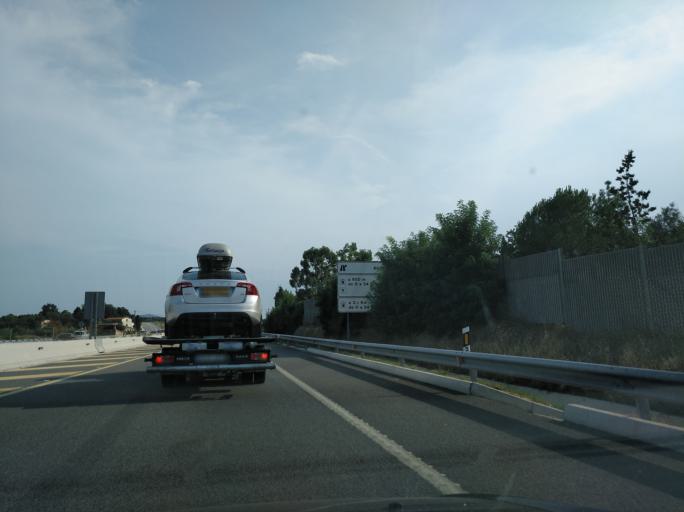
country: ES
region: Catalonia
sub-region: Provincia de Girona
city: Sils
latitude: 41.8112
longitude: 2.7639
